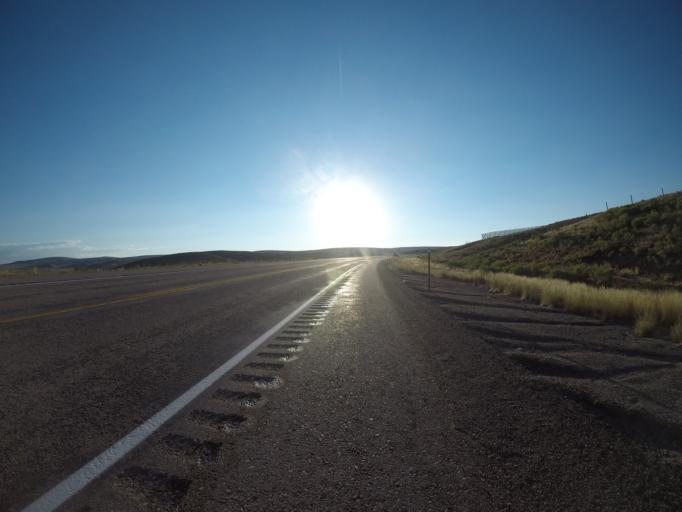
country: US
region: Wyoming
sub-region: Lincoln County
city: Kemmerer
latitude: 41.8746
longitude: -110.4865
